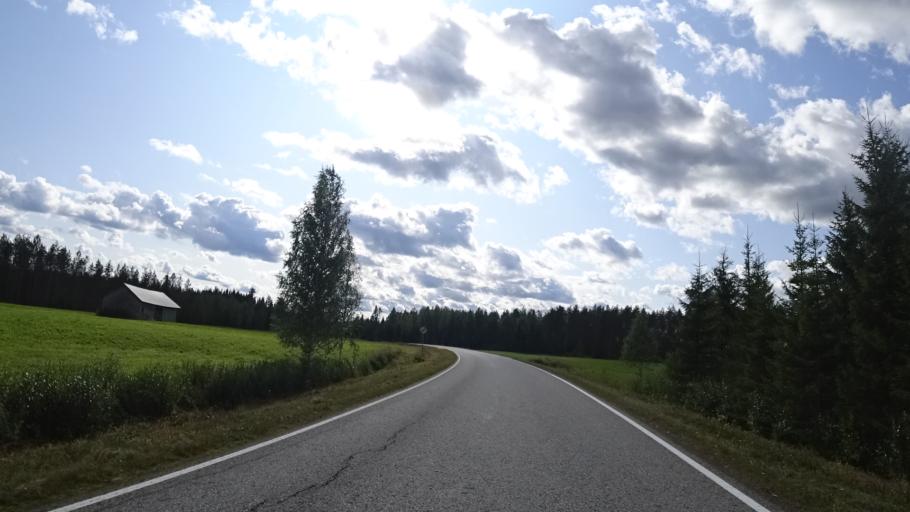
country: RU
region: Republic of Karelia
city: Vyartsilya
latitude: 62.2690
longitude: 30.7857
